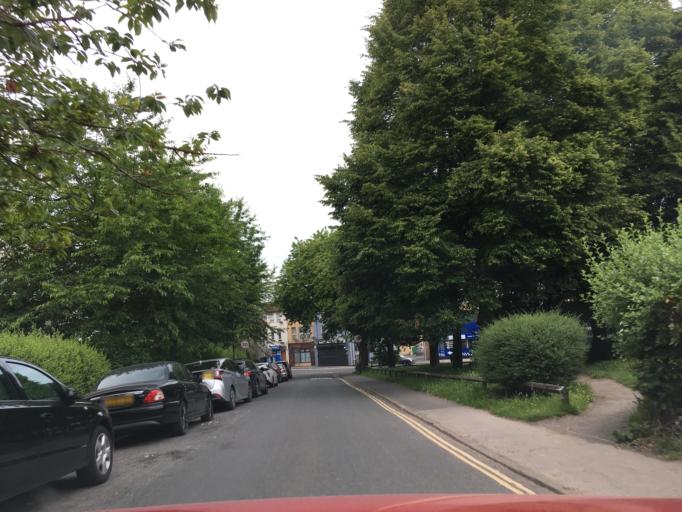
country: GB
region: England
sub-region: Bristol
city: Bristol
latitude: 51.4573
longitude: -2.5627
